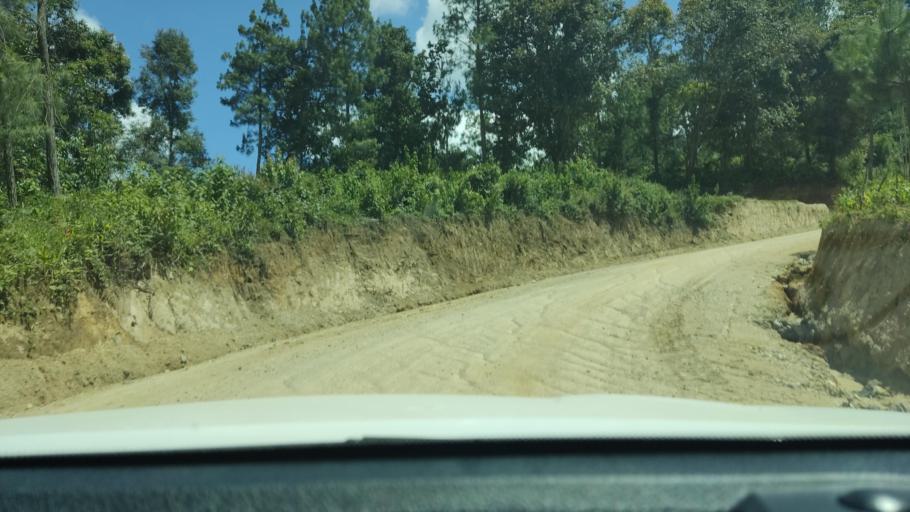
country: GT
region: Chimaltenango
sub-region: Municipio de San Juan Comalapa
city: Comalapa
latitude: 14.7618
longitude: -90.8839
